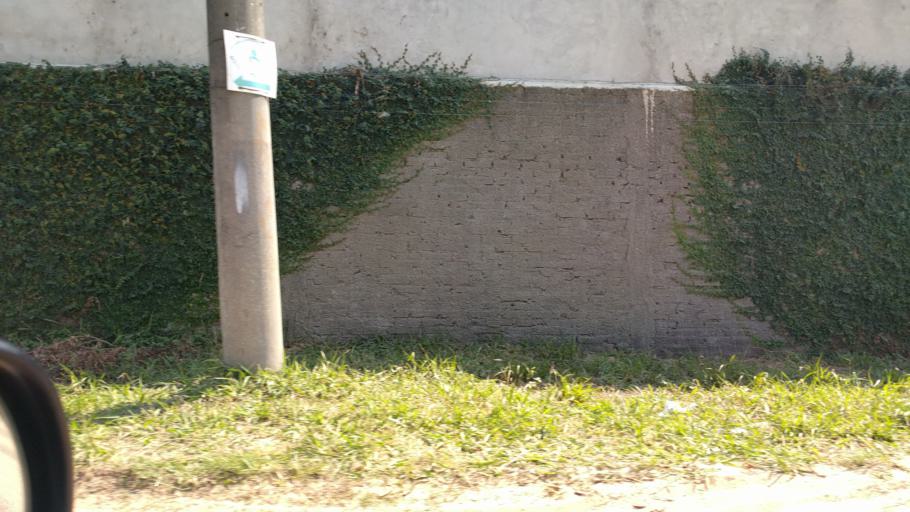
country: BO
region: Santa Cruz
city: Santa Cruz de la Sierra
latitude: -17.7536
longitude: -63.2228
